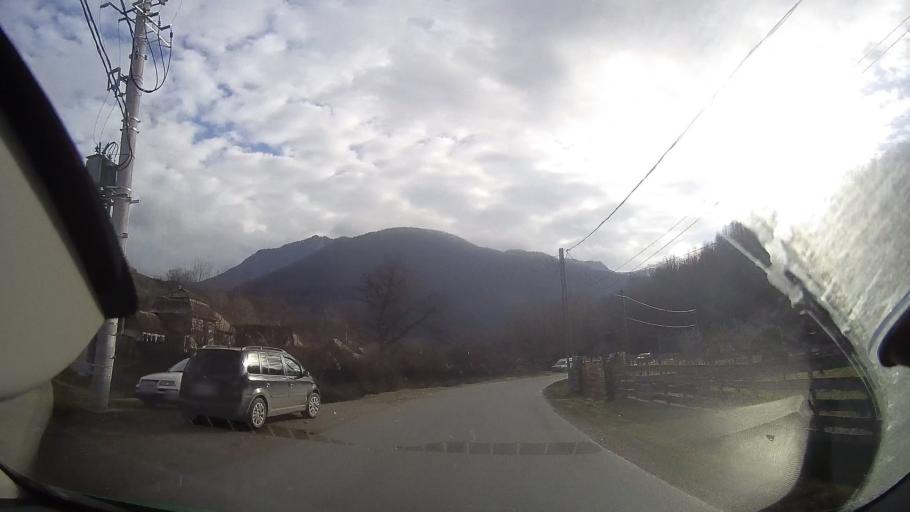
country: RO
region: Alba
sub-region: Comuna Ocolis
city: Ocolis
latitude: 46.4732
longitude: 23.4719
